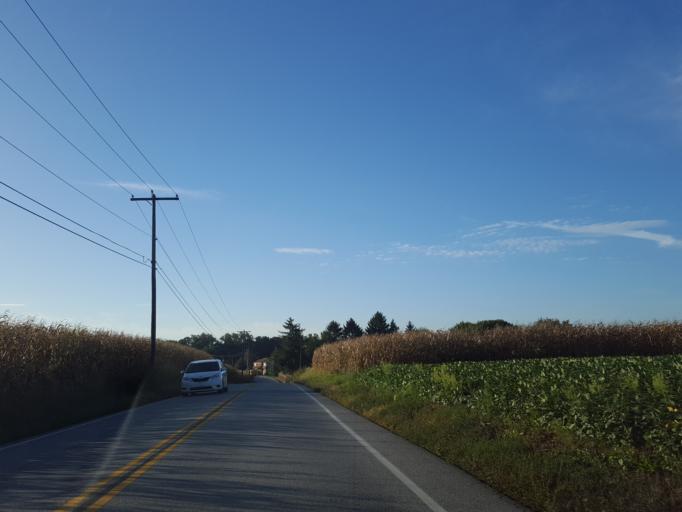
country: US
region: Pennsylvania
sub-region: York County
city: Stonybrook
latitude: 39.9687
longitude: -76.6146
